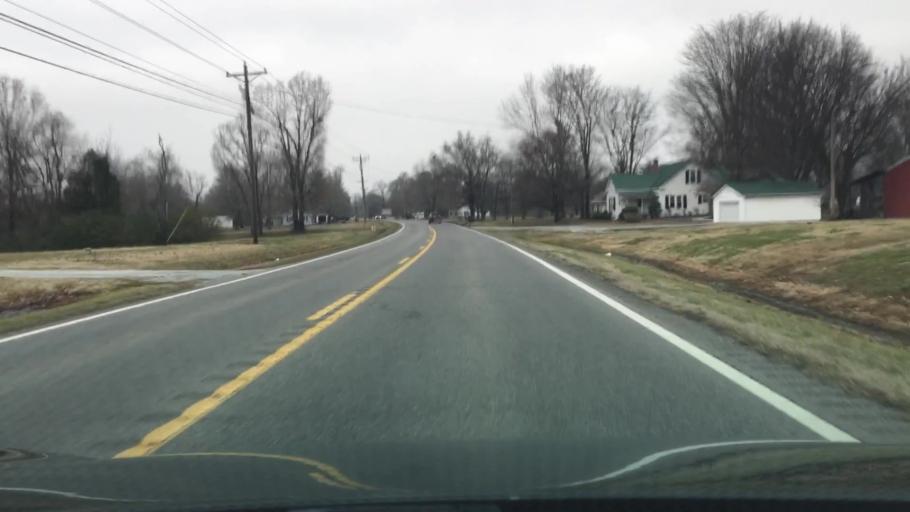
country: US
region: Kentucky
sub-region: Marshall County
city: Calvert City
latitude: 36.9683
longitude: -88.3860
